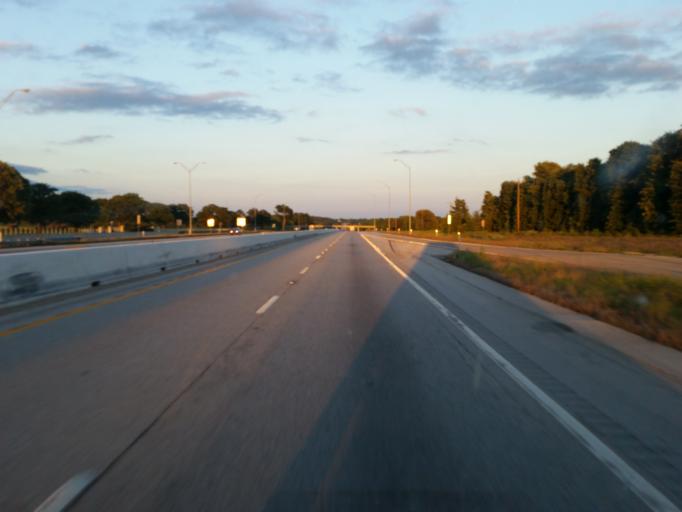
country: US
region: Texas
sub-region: Van Zandt County
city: Van
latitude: 32.4926
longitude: -95.5588
